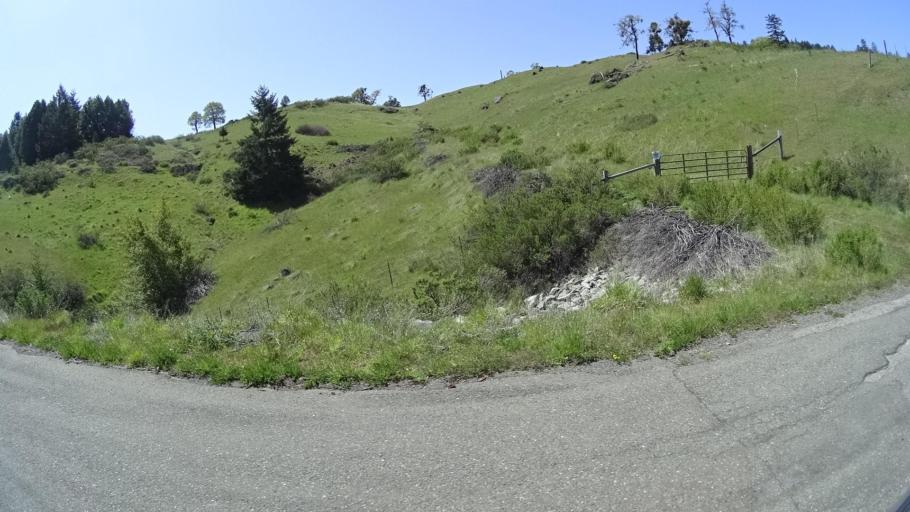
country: US
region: California
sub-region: Humboldt County
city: Redway
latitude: 40.1103
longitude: -123.6711
